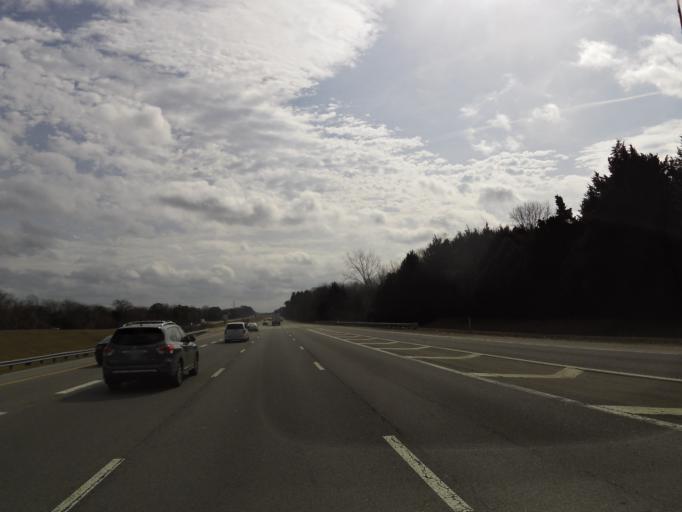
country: US
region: Tennessee
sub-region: Rutherford County
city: Smyrna
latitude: 35.9325
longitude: -86.5301
